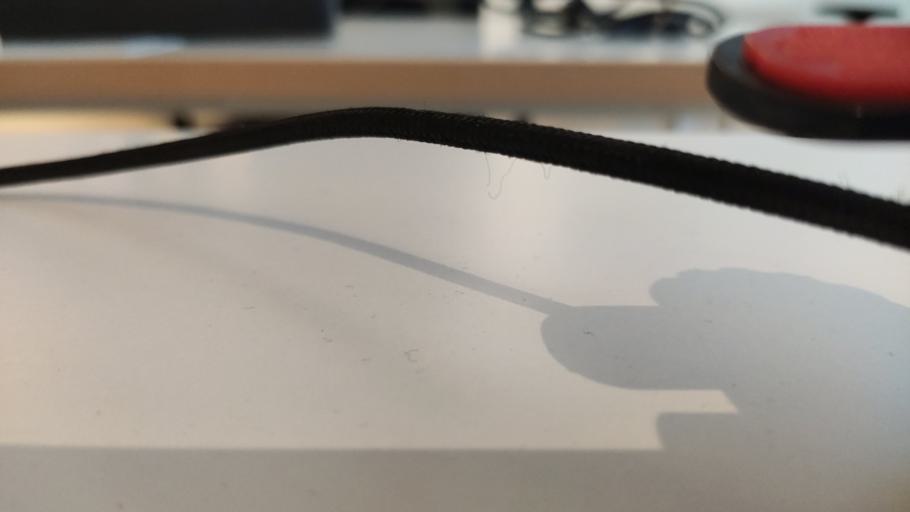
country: RU
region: Moskovskaya
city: Novopetrovskoye
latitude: 55.9163
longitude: 36.4396
